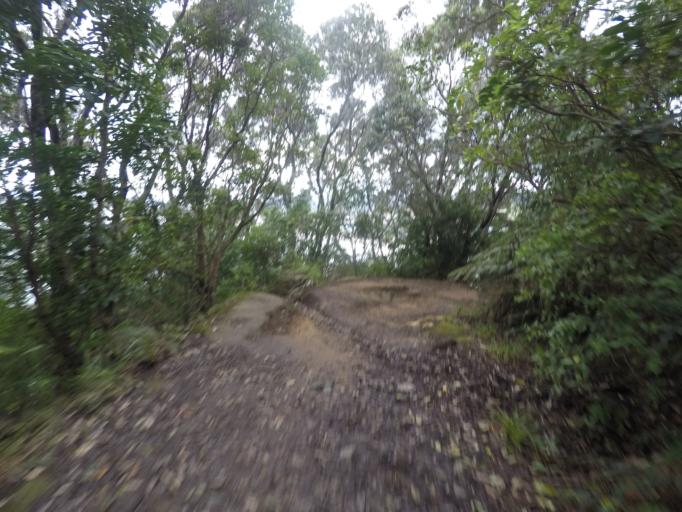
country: NZ
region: Bay of Plenty
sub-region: Western Bay of Plenty District
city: Waihi Beach
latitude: -37.3932
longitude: 175.9410
